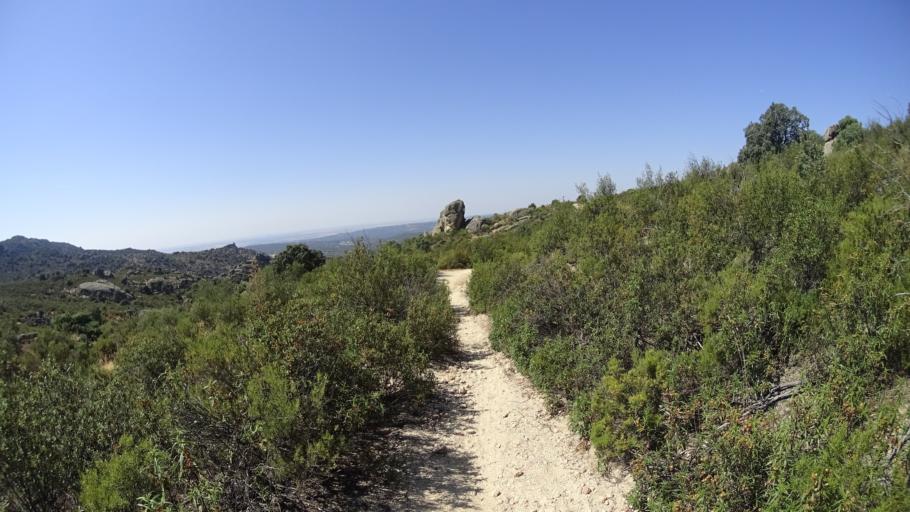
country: ES
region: Madrid
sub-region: Provincia de Madrid
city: Hoyo de Manzanares
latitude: 40.6420
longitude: -3.9389
